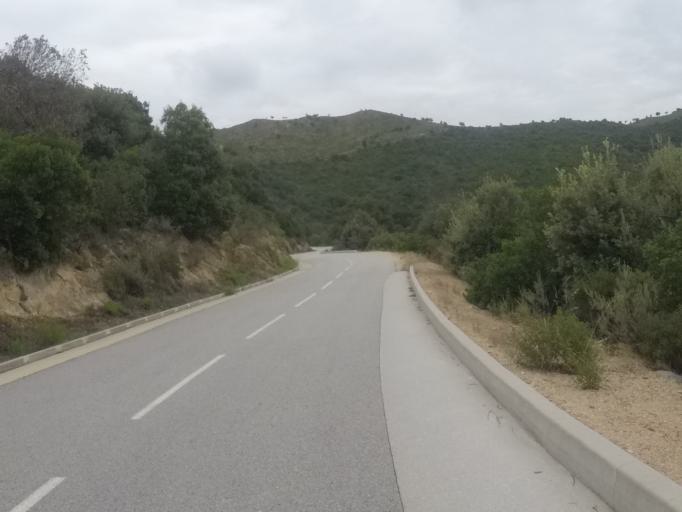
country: FR
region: Corsica
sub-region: Departement de la Corse-du-Sud
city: Pietrosella
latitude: 41.7725
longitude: 8.8152
